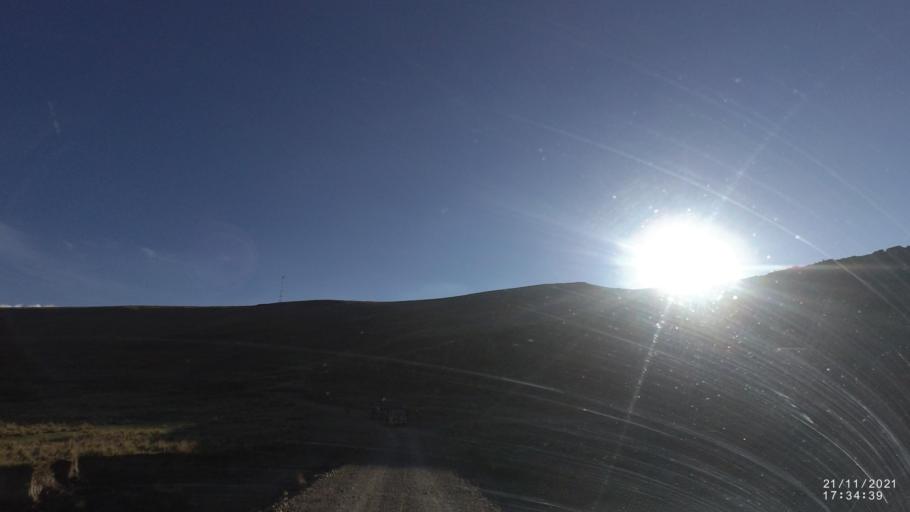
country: BO
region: Cochabamba
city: Cochabamba
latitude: -17.1984
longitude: -66.2464
